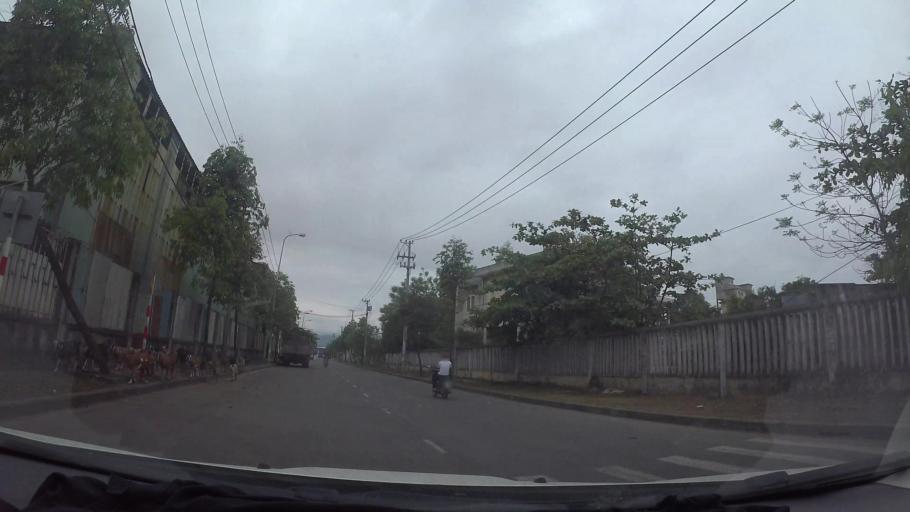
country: VN
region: Da Nang
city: Lien Chieu
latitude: 16.0845
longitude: 108.1393
